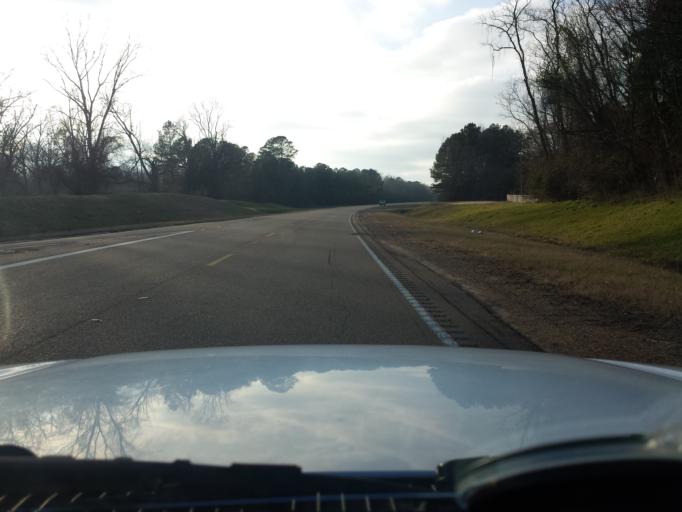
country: US
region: Mississippi
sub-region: Yazoo County
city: Yazoo City
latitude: 32.8316
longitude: -90.3269
